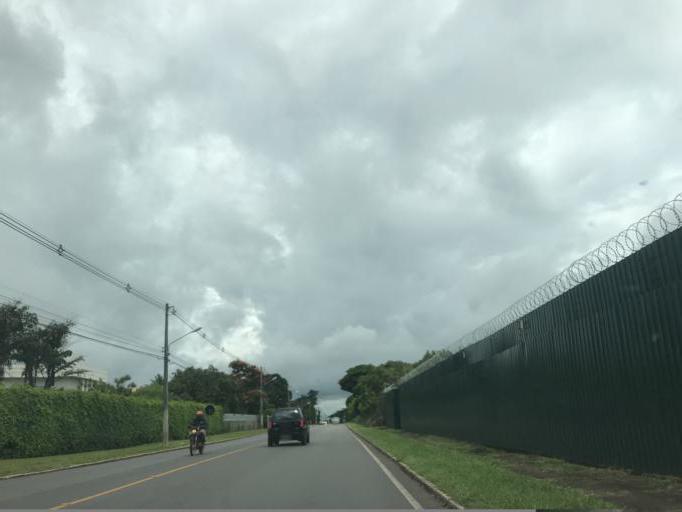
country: BR
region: Federal District
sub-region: Brasilia
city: Brasilia
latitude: -15.8523
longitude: -47.8800
